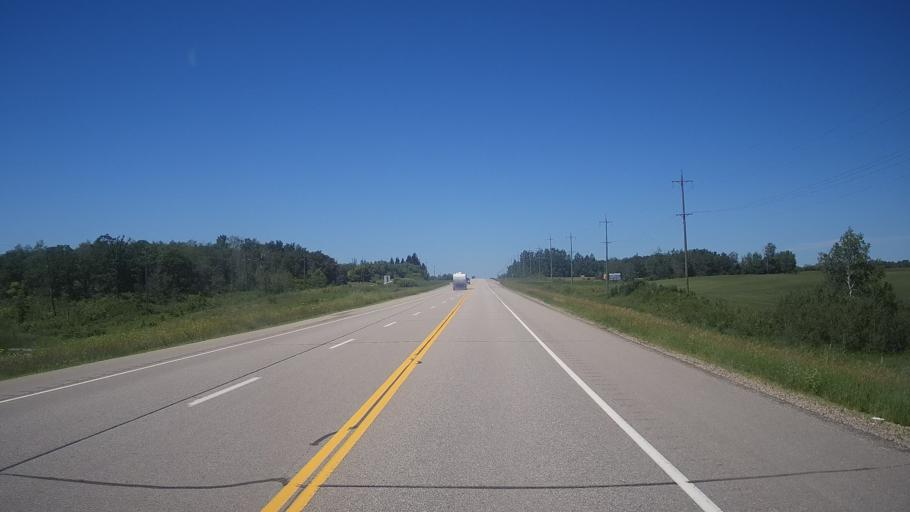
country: CA
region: Manitoba
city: Neepawa
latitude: 50.2254
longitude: -99.3600
